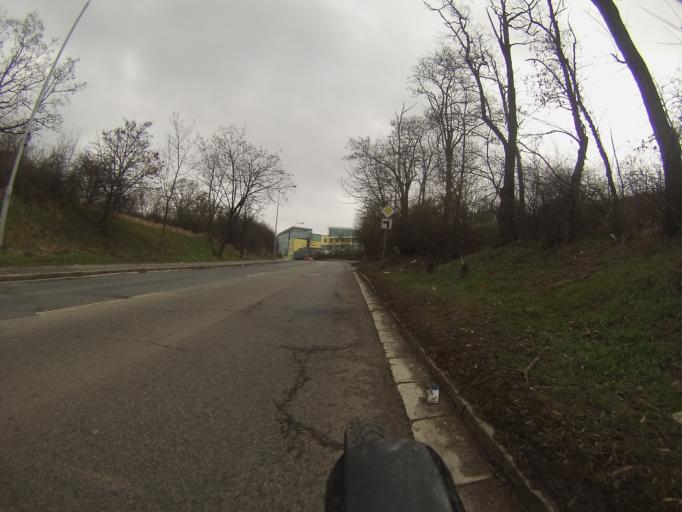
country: CZ
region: South Moravian
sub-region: Mesto Brno
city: Brno
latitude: 49.1968
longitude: 16.6587
